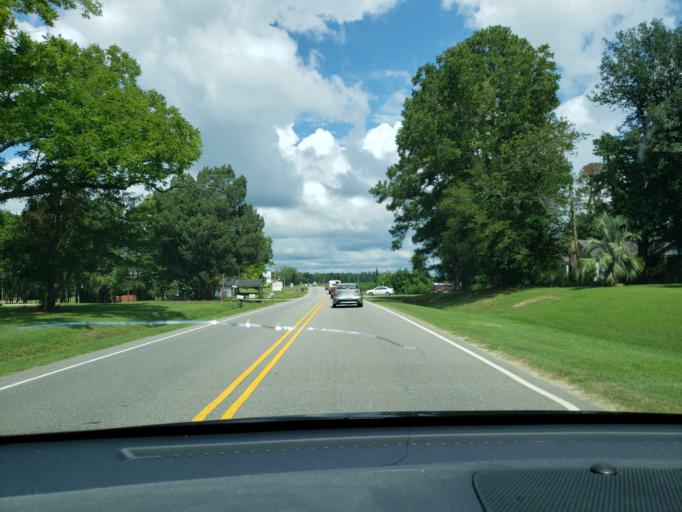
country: US
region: North Carolina
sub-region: Columbus County
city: Brunswick
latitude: 34.2707
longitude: -78.7420
